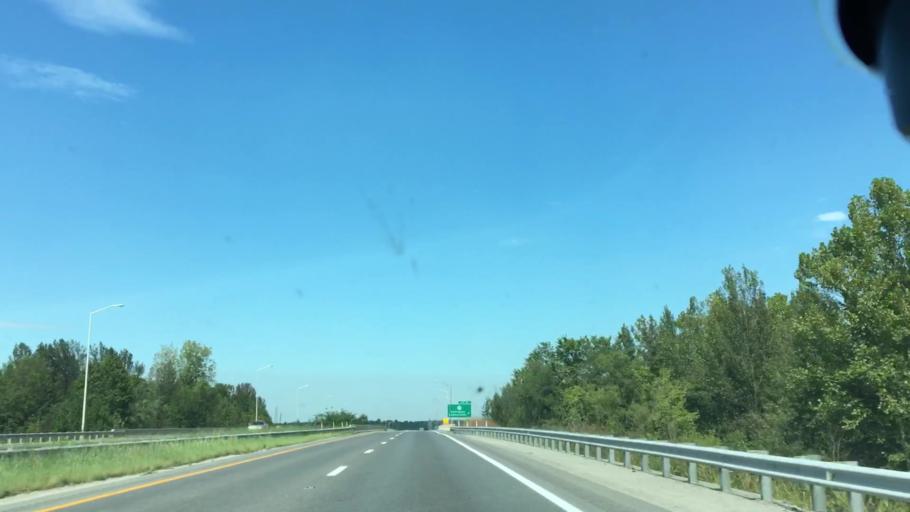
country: US
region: Kentucky
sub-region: Hopkins County
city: Earlington
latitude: 37.2901
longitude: -87.4599
